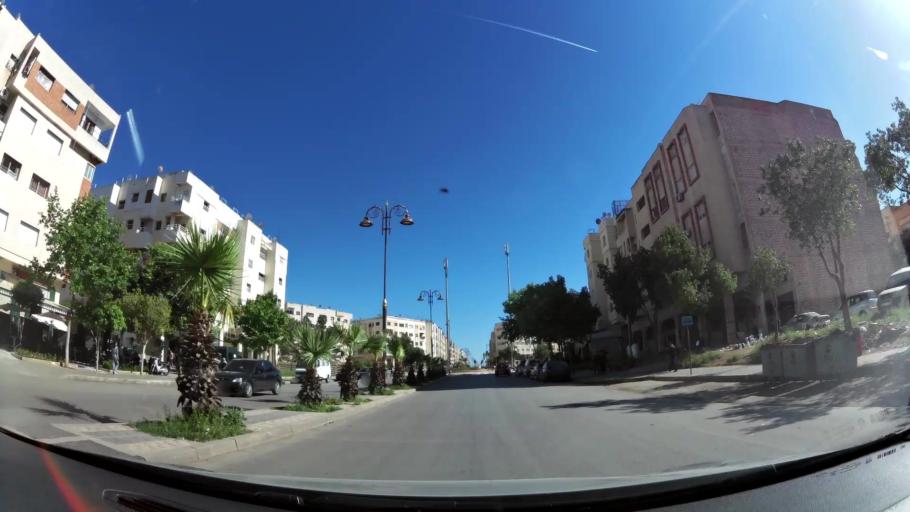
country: MA
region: Fes-Boulemane
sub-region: Fes
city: Fes
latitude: 34.0156
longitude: -4.9705
